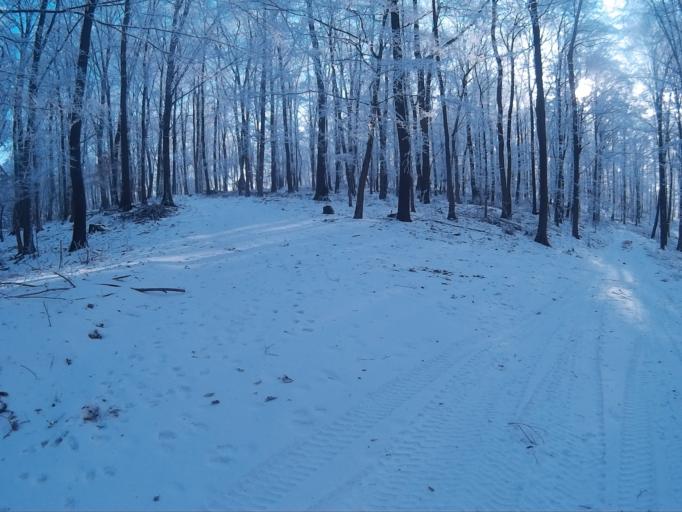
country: HU
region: Borsod-Abauj-Zemplen
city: Szendro
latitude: 48.4917
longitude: 20.7443
